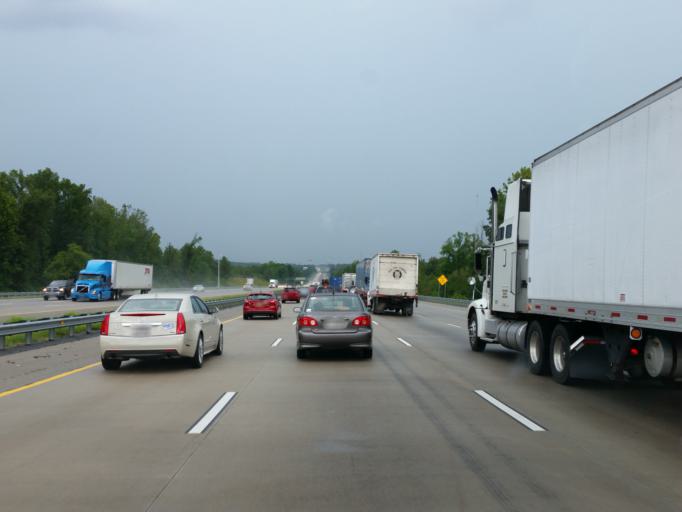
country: US
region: Georgia
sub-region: Peach County
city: Byron
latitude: 32.7077
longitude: -83.7331
